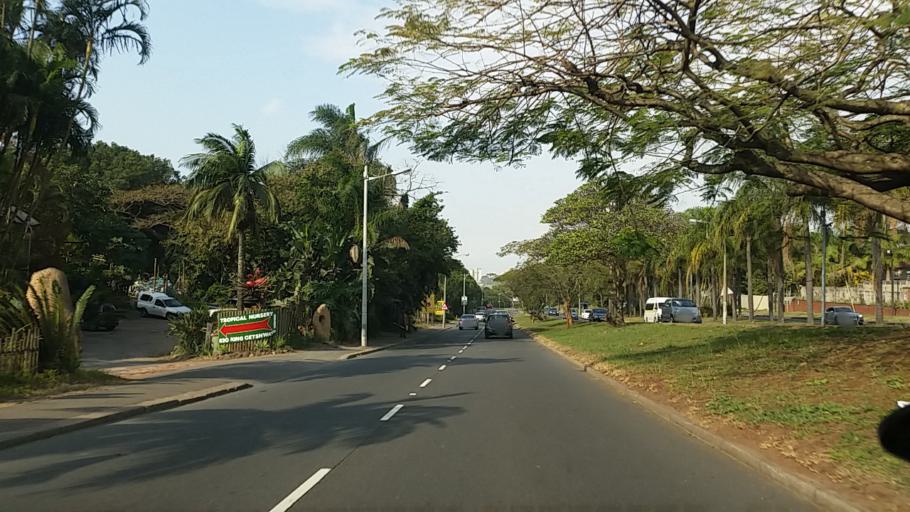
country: ZA
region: KwaZulu-Natal
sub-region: eThekwini Metropolitan Municipality
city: Berea
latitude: -29.8363
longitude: 30.9714
